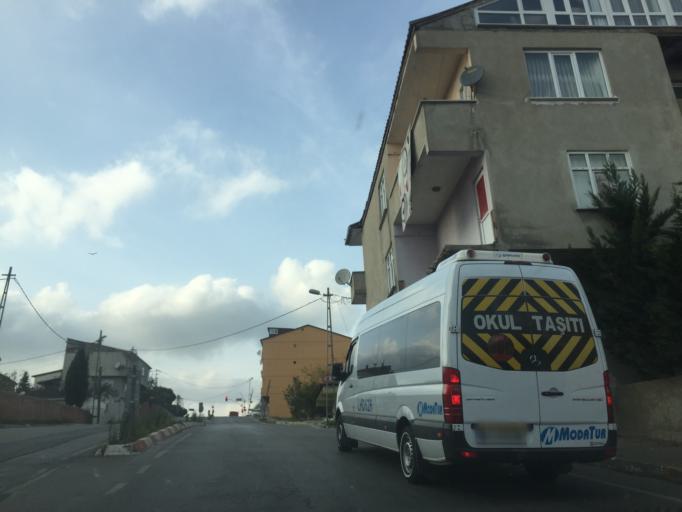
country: TR
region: Istanbul
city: Sultanbeyli
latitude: 40.9484
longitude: 29.2978
